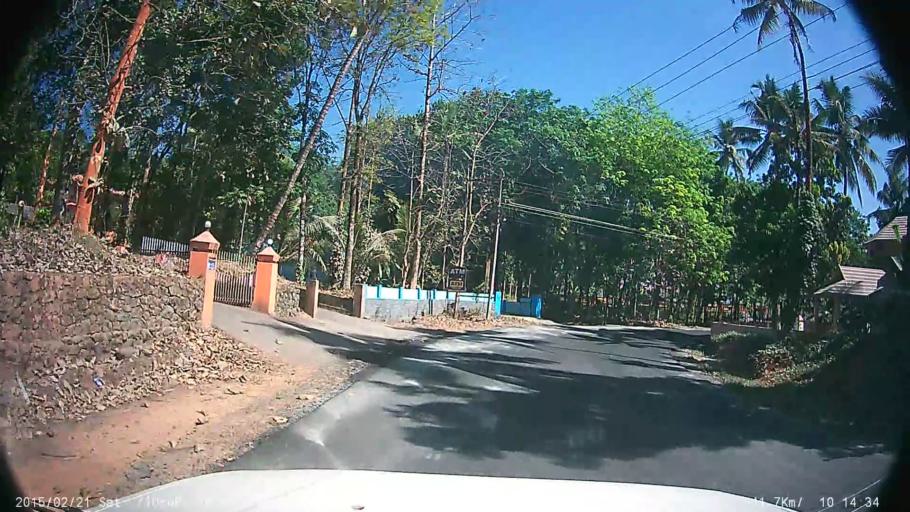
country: IN
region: Kerala
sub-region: Ernakulam
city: Muvattupuzha
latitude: 9.8852
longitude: 76.6383
